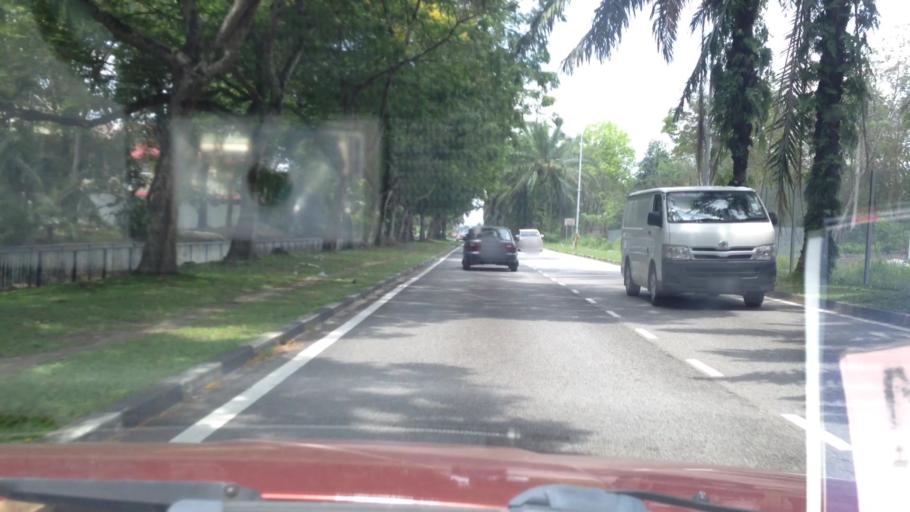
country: MY
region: Selangor
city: Kampung Baru Subang
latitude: 3.1724
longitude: 101.5500
